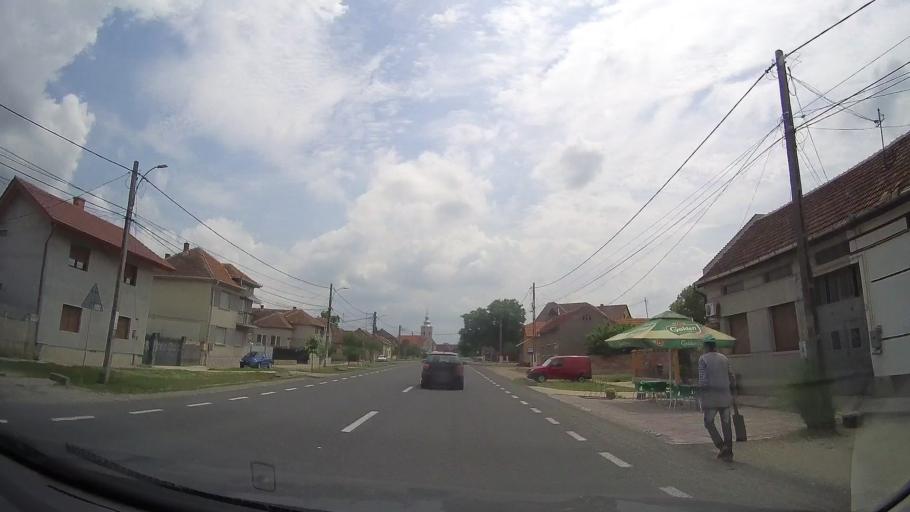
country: RO
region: Timis
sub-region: Comuna Costeiu
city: Costeiu
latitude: 45.7335
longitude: 21.8632
